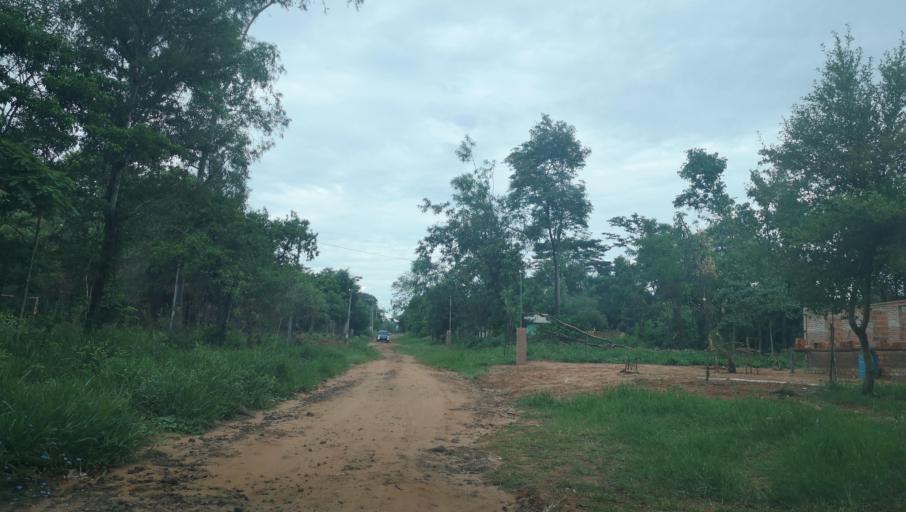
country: PY
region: San Pedro
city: Capiibary
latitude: -24.7408
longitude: -56.0261
